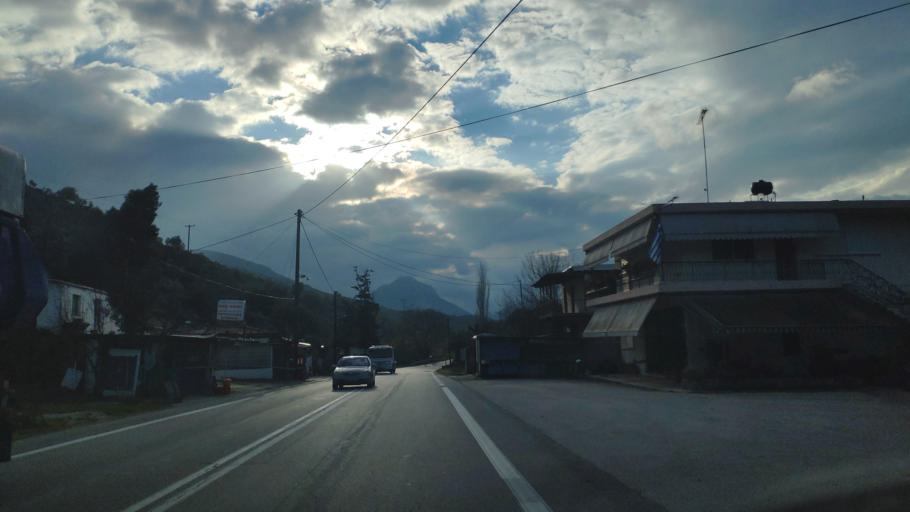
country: GR
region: Peloponnese
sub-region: Nomos Korinthias
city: Nemea
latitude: 37.7820
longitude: 22.7215
